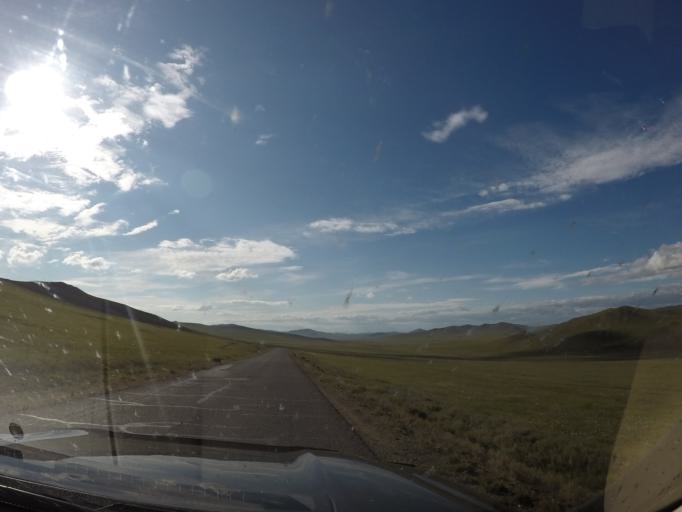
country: MN
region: Hentiy
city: Modot
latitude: 47.8079
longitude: 108.8082
